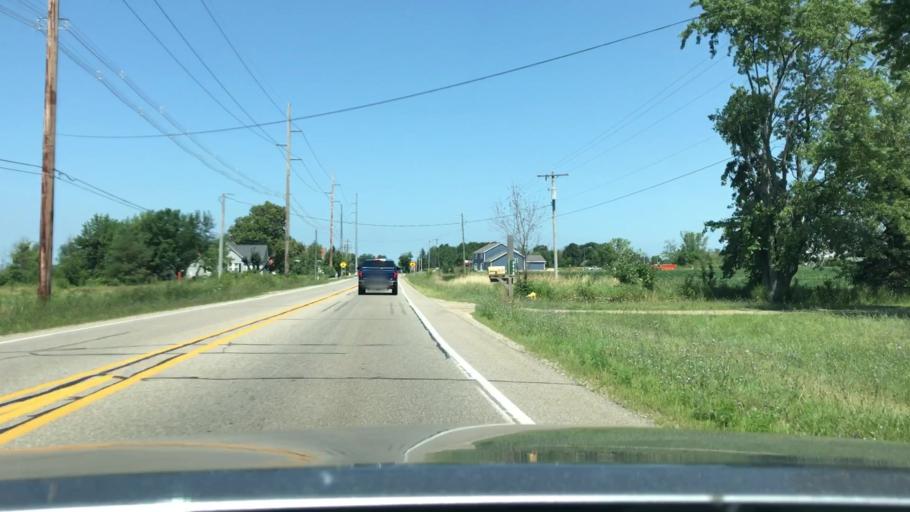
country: US
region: Michigan
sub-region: Ottawa County
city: Holland
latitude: 42.8382
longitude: -86.0788
